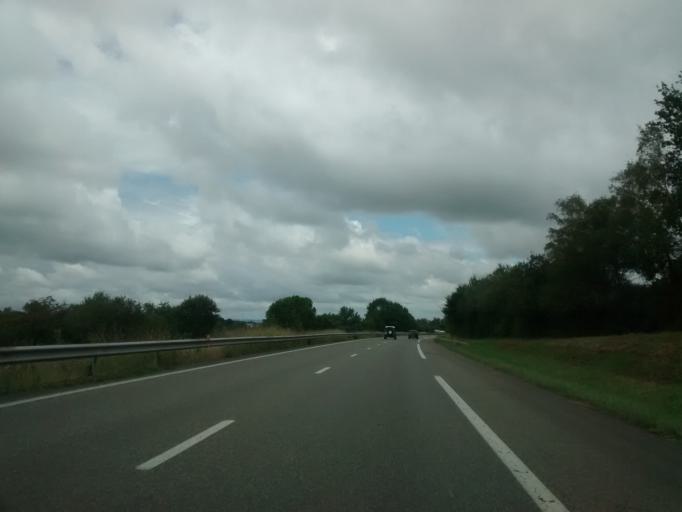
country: FR
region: Aquitaine
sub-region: Departement des Pyrenees-Atlantiques
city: Poey-de-Lescar
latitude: 43.3631
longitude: -0.4744
